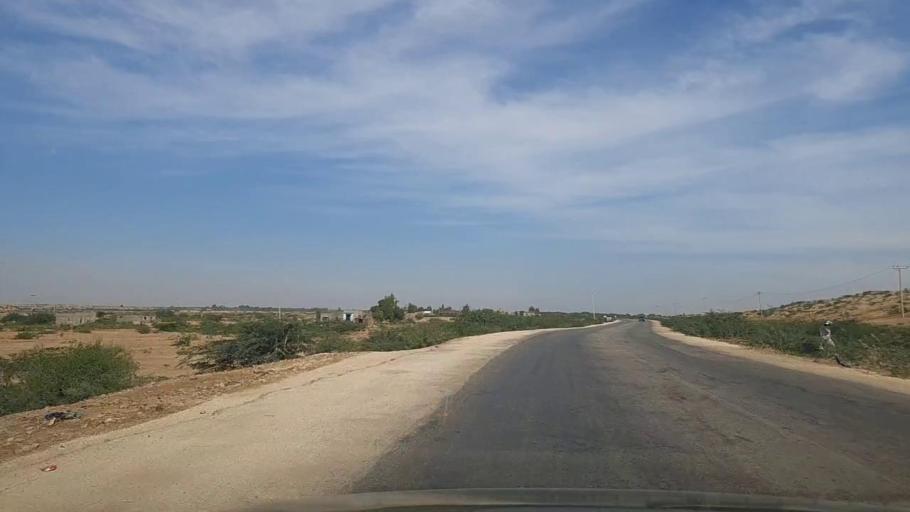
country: PK
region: Sindh
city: Daro Mehar
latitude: 24.9877
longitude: 68.1399
